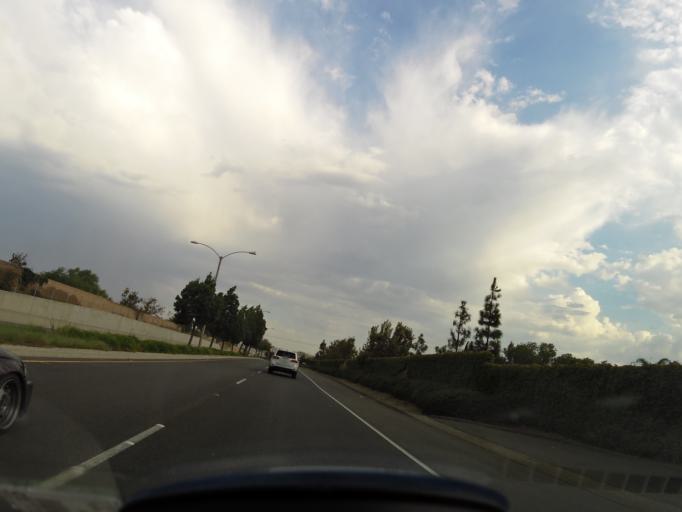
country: US
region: California
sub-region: Orange County
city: Yorba Linda
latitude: 33.8823
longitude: -117.8099
